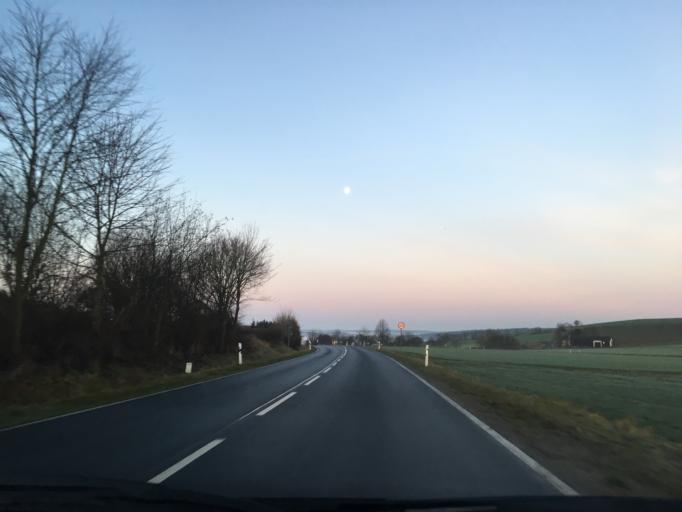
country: DE
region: Hesse
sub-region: Regierungsbezirk Kassel
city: Hofbieber
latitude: 50.5925
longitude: 9.8405
